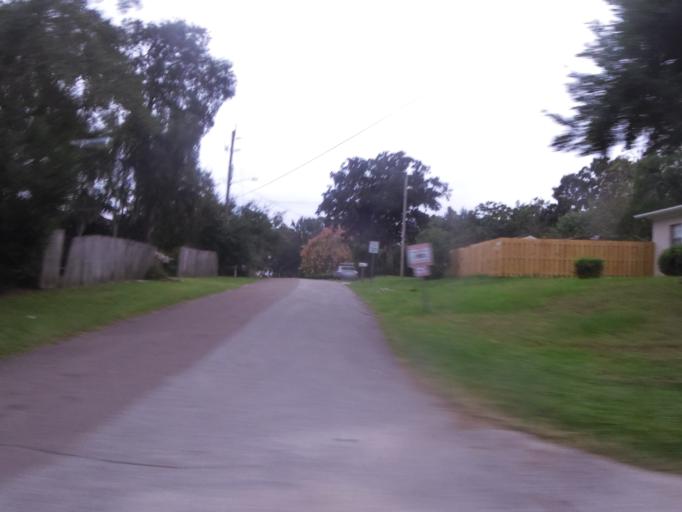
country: US
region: Florida
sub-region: Clay County
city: Bellair-Meadowbrook Terrace
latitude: 30.2745
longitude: -81.7418
